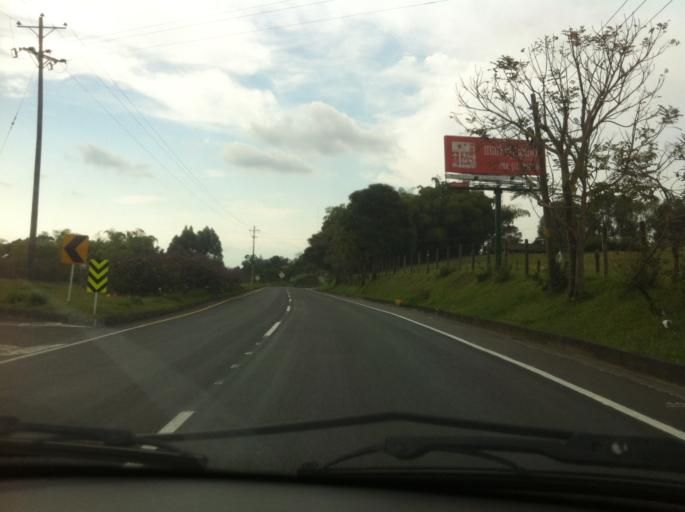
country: CO
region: Quindio
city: Filandia
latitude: 4.7396
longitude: -75.6572
